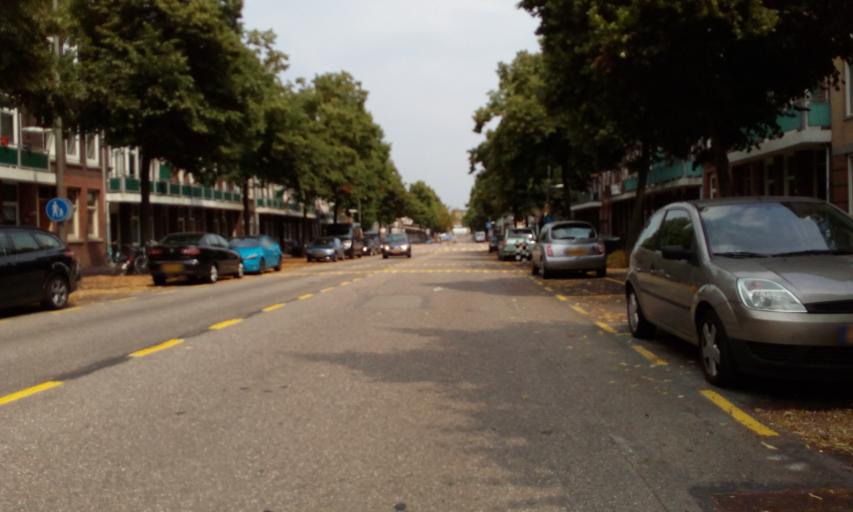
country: NL
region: South Holland
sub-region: Gemeente Schiedam
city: Schiedam
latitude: 51.9154
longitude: 4.4118
